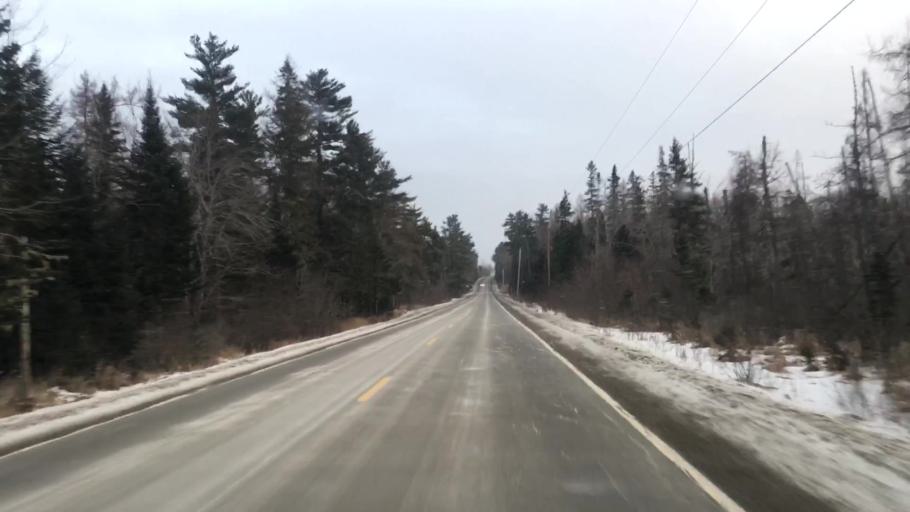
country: US
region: Maine
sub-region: Hancock County
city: Ellsworth
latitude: 44.6765
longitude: -68.3531
